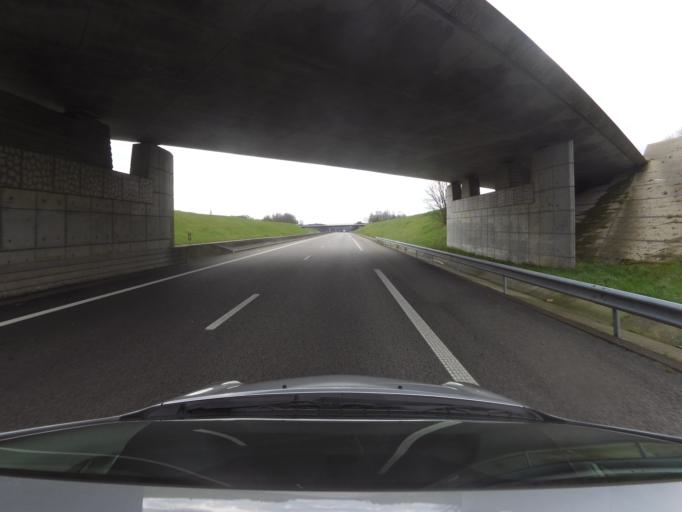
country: FR
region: Haute-Normandie
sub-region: Departement de la Seine-Maritime
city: Saint-Aubin-Routot
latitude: 49.5207
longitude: 0.3028
